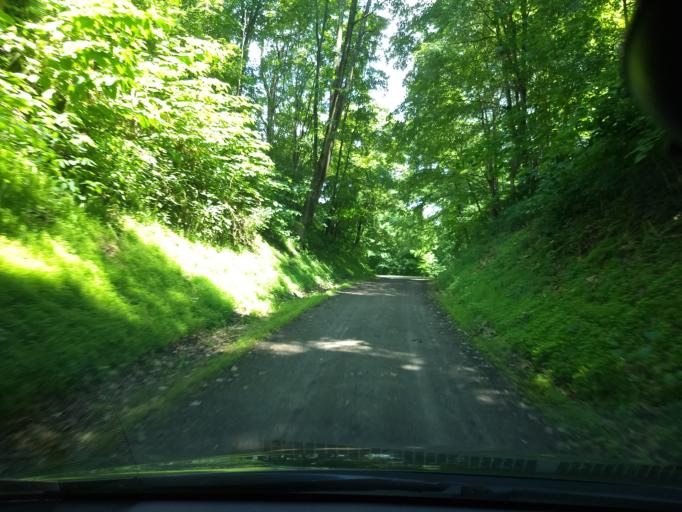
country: US
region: Pennsylvania
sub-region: Westmoreland County
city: Avonmore
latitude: 40.5231
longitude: -79.4935
